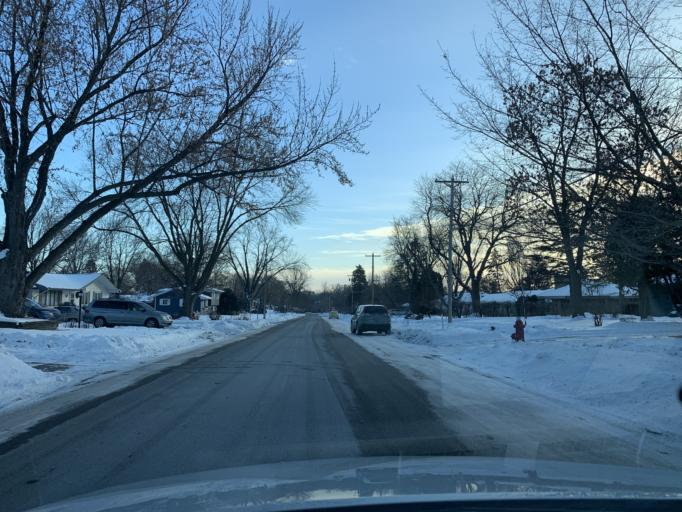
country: US
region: Minnesota
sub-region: Hennepin County
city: Minnetonka Mills
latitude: 44.9582
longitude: -93.3962
